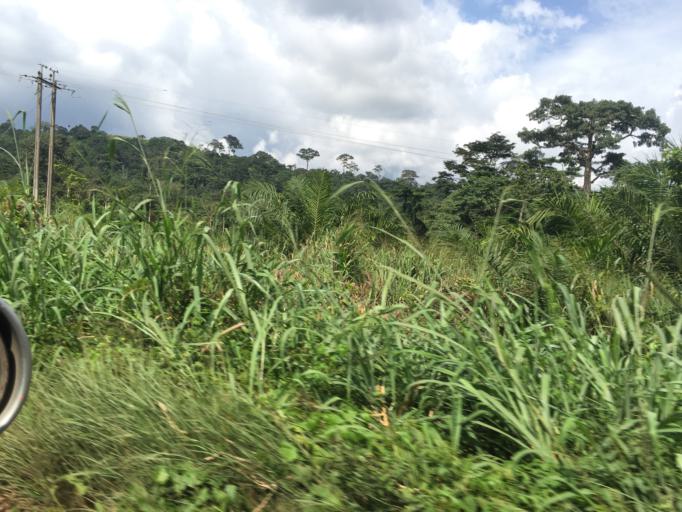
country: GH
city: Mpraeso
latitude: 6.6056
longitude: -0.7396
